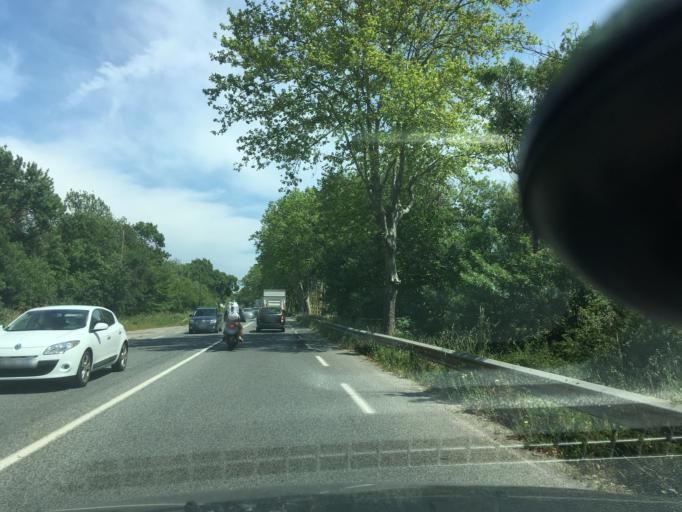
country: FR
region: Provence-Alpes-Cote d'Azur
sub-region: Departement du Var
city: Roquebrune-sur-Argens
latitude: 43.4619
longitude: 6.6511
